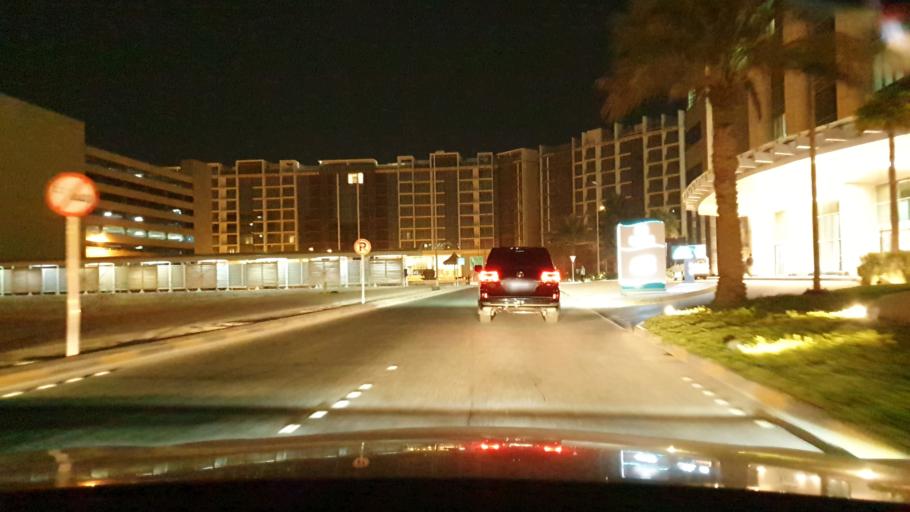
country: BH
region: Manama
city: Manama
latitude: 26.2368
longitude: 50.5728
